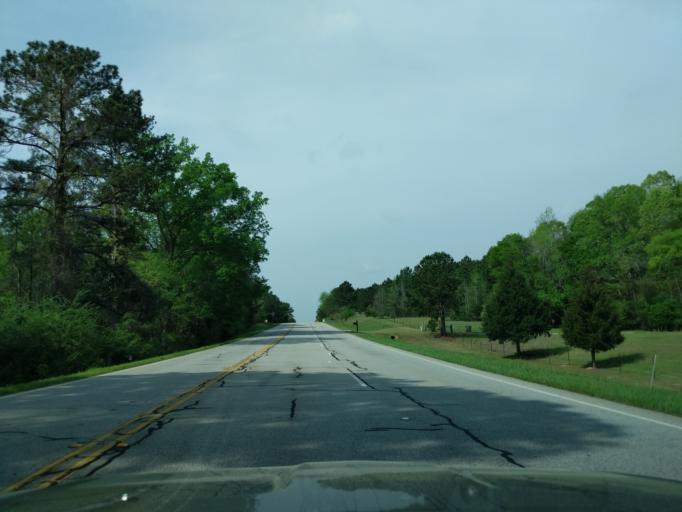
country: US
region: Georgia
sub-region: Lincoln County
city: Lincolnton
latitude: 33.8481
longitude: -82.4004
